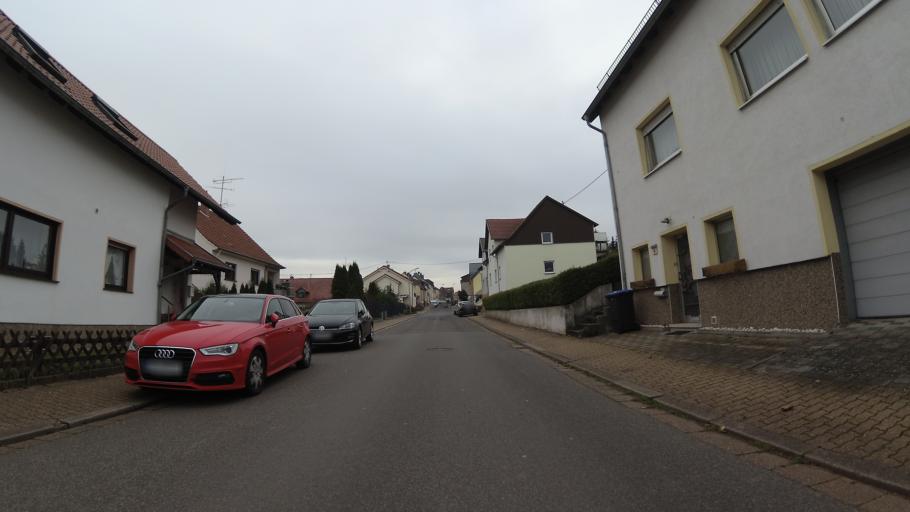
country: DE
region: Saarland
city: Merchweiler
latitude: 49.3542
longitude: 7.0547
